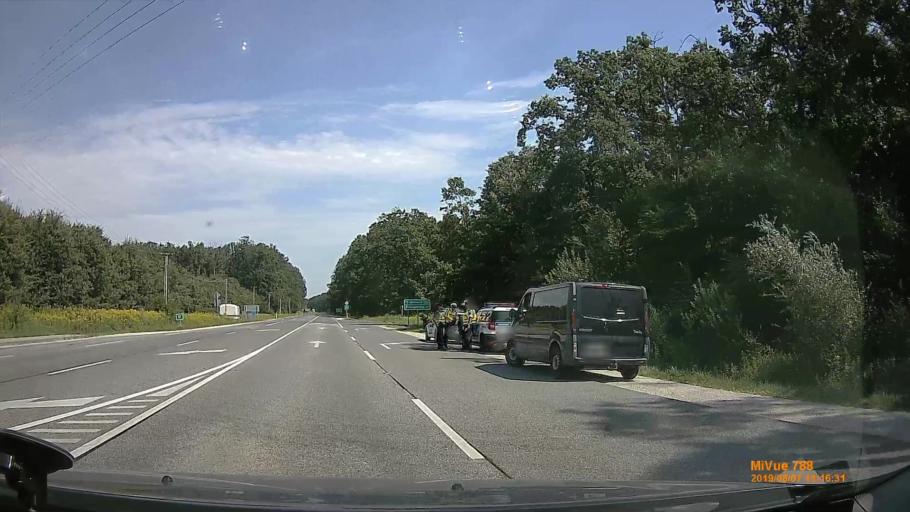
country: HU
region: Zala
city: Lenti
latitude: 46.7286
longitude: 16.5513
